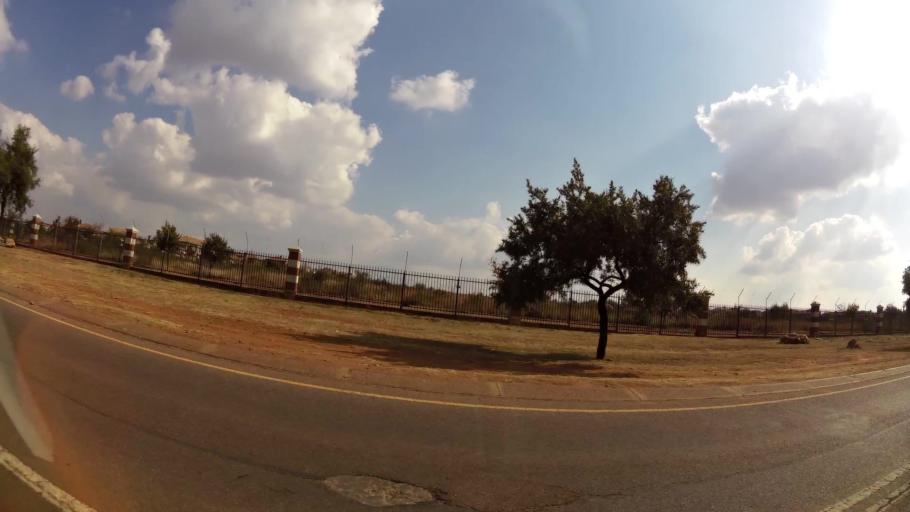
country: ZA
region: Gauteng
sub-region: City of Tshwane Metropolitan Municipality
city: Centurion
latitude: -25.8573
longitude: 28.2477
